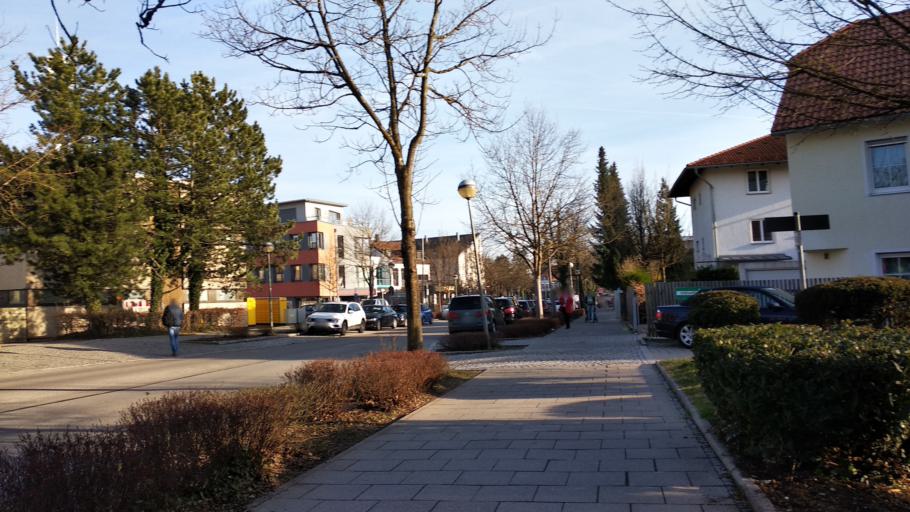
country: DE
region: Bavaria
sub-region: Upper Bavaria
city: Unterhaching
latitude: 48.0636
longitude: 11.6138
